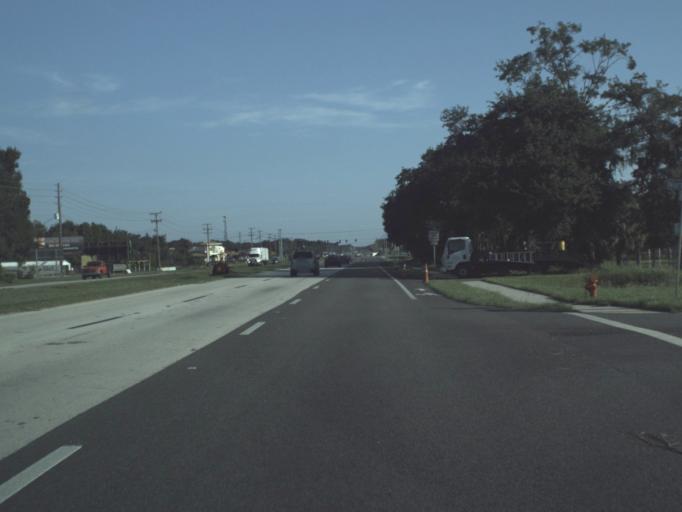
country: US
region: Florida
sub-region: Polk County
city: Gibsonia
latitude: 28.1243
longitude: -81.9734
